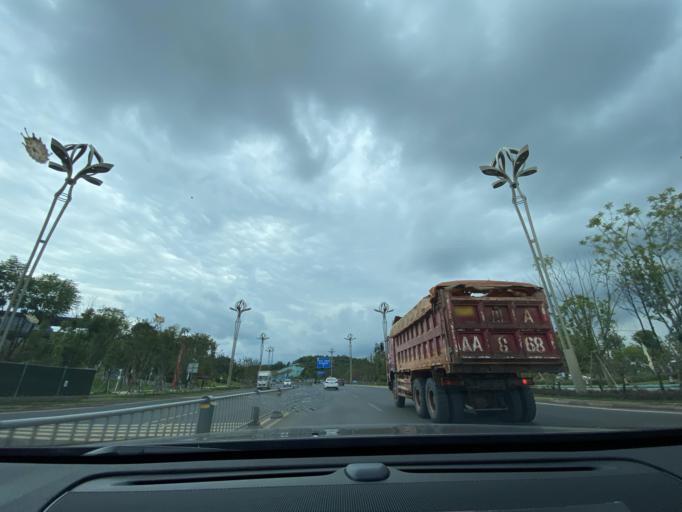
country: CN
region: Sichuan
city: Jiancheng
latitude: 30.4965
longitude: 104.4634
